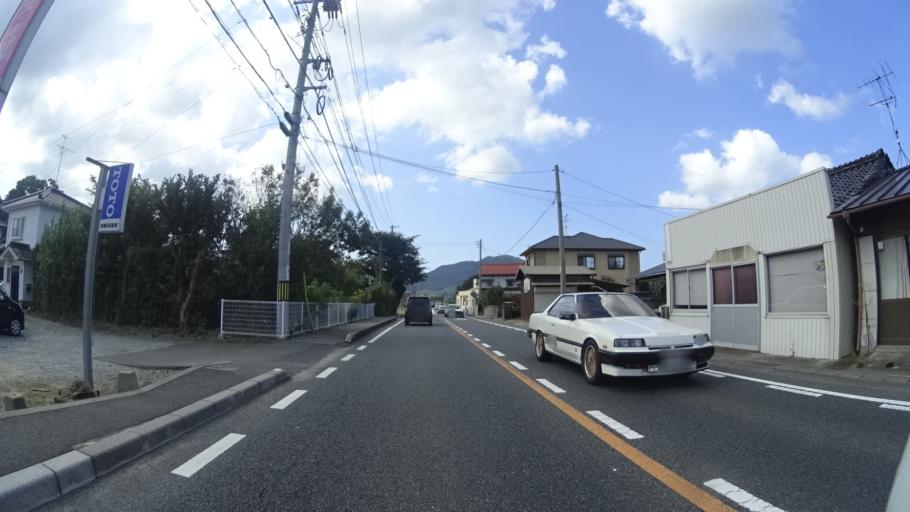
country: JP
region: Yamaguchi
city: Shimonoseki
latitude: 34.1241
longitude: 130.9129
